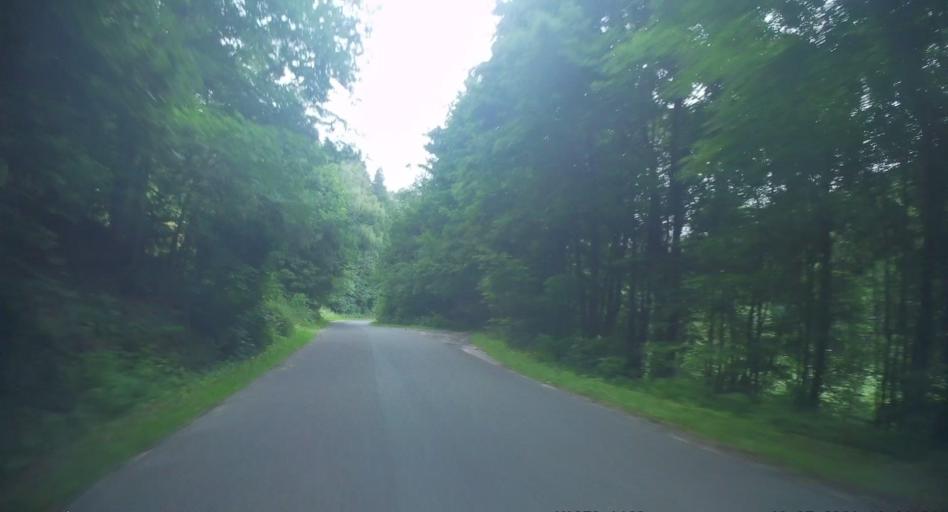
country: PL
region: Lower Silesian Voivodeship
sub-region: Powiat klodzki
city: Ludwikowice Klodzkie
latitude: 50.6341
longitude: 16.4634
